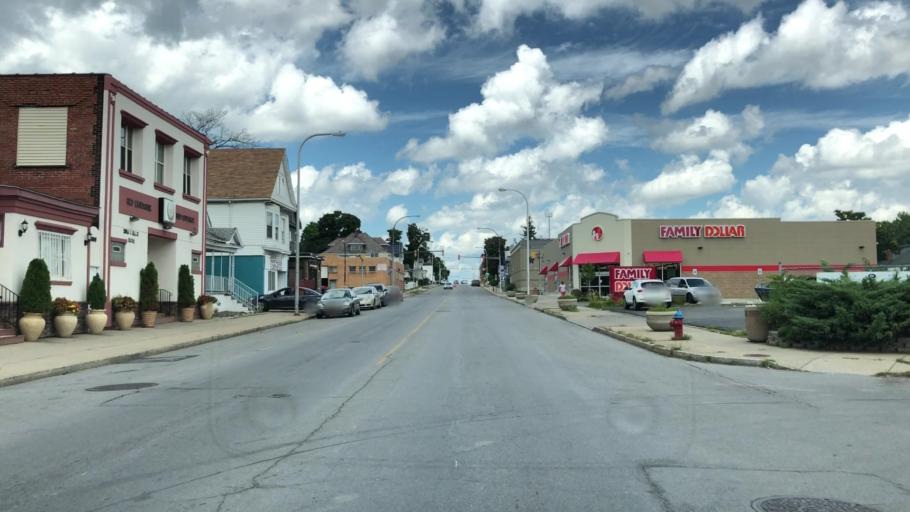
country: US
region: New York
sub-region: Erie County
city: Buffalo
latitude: 42.8992
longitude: -78.8540
